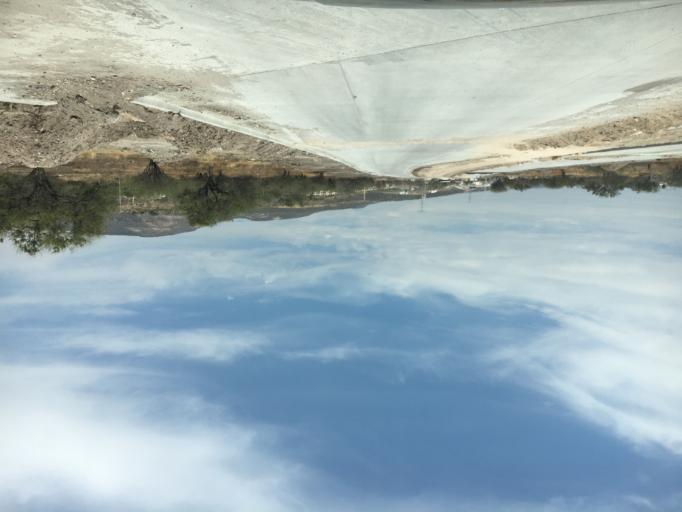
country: MX
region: Guanajuato
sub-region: Leon
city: Fraccionamiento Paraiso Real
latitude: 21.1194
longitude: -101.5915
